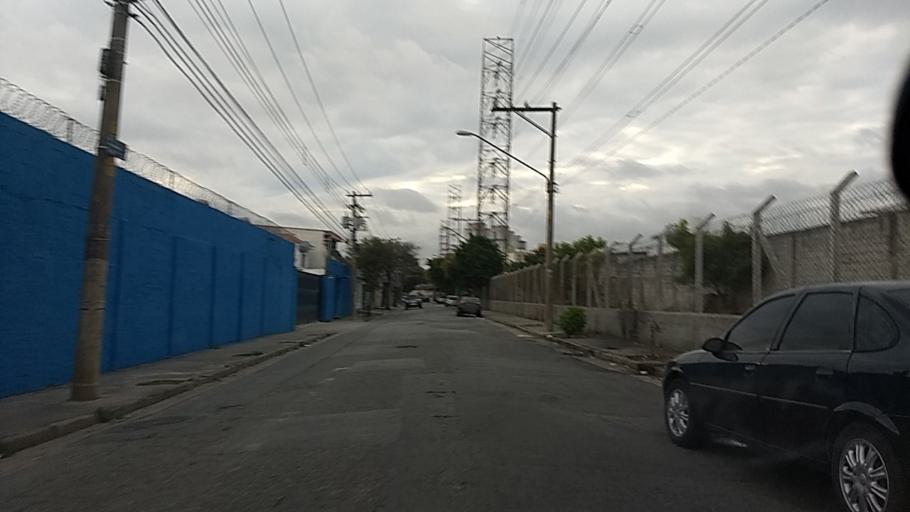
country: BR
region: Sao Paulo
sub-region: Sao Paulo
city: Sao Paulo
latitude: -23.5152
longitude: -46.6007
